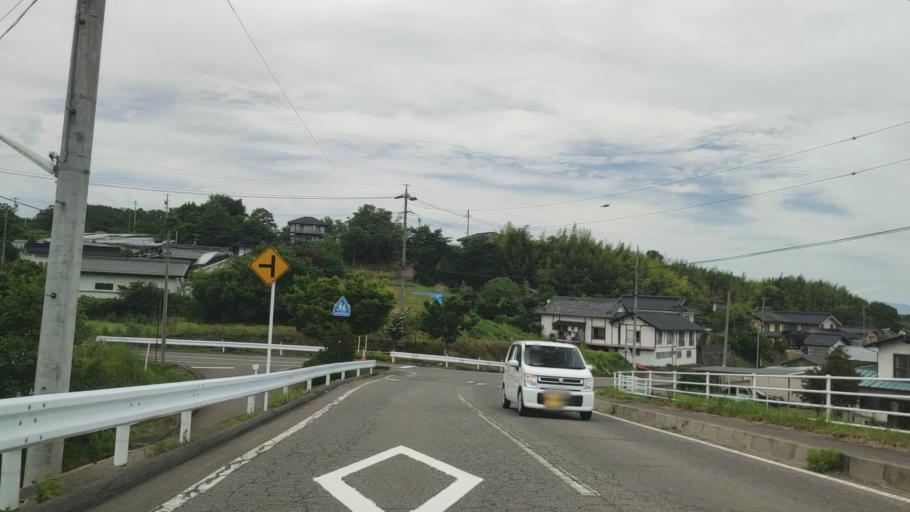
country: JP
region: Nagano
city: Kamimaruko
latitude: 36.2772
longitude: 138.3172
